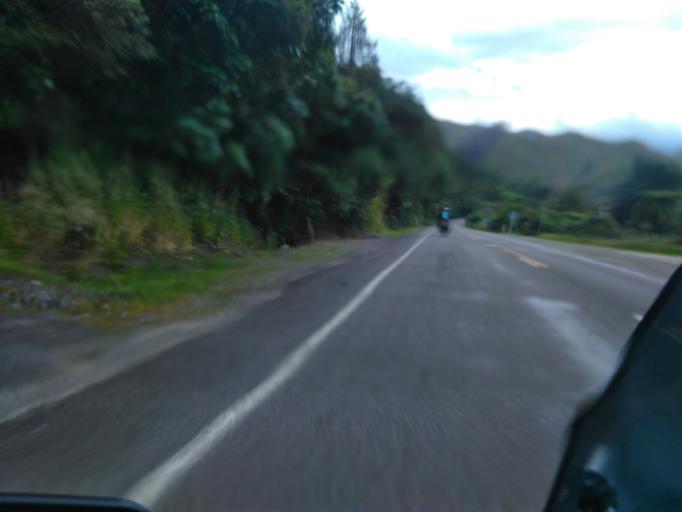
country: NZ
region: Bay of Plenty
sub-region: Opotiki District
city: Opotiki
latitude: -38.2575
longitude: 177.2988
